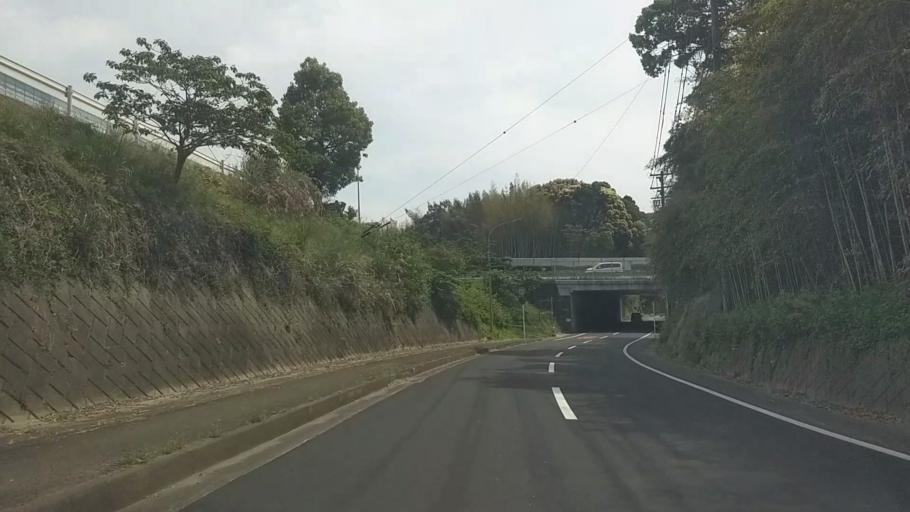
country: JP
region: Shizuoka
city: Kosai-shi
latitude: 34.7752
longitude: 137.6378
